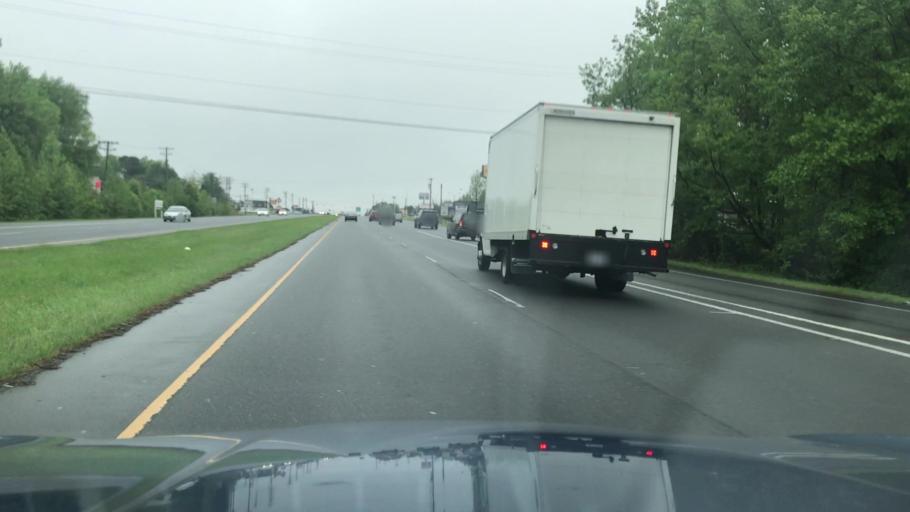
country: US
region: North Carolina
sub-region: Mecklenburg County
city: Matthews
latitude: 35.1225
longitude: -80.7018
